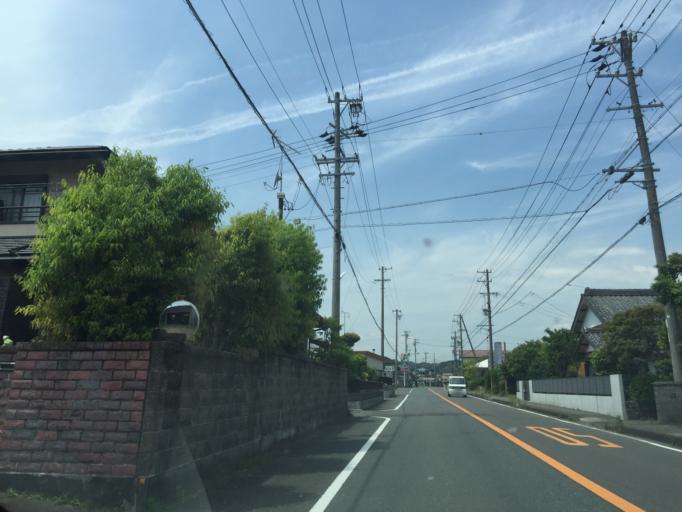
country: JP
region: Shizuoka
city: Mori
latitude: 34.8006
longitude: 137.9587
